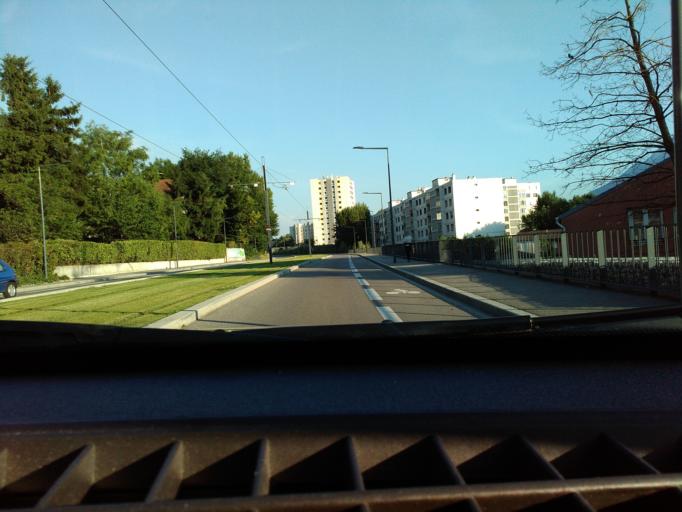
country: FR
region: Rhone-Alpes
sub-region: Departement de l'Isere
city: Saint-Egreve
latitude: 45.2392
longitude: 5.6731
